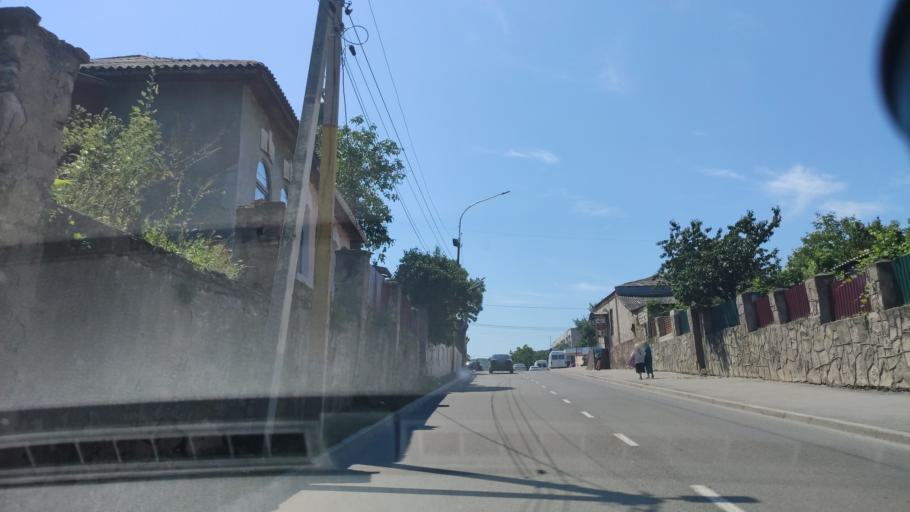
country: MD
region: Raionul Soroca
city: Soroca
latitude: 48.1630
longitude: 28.3020
